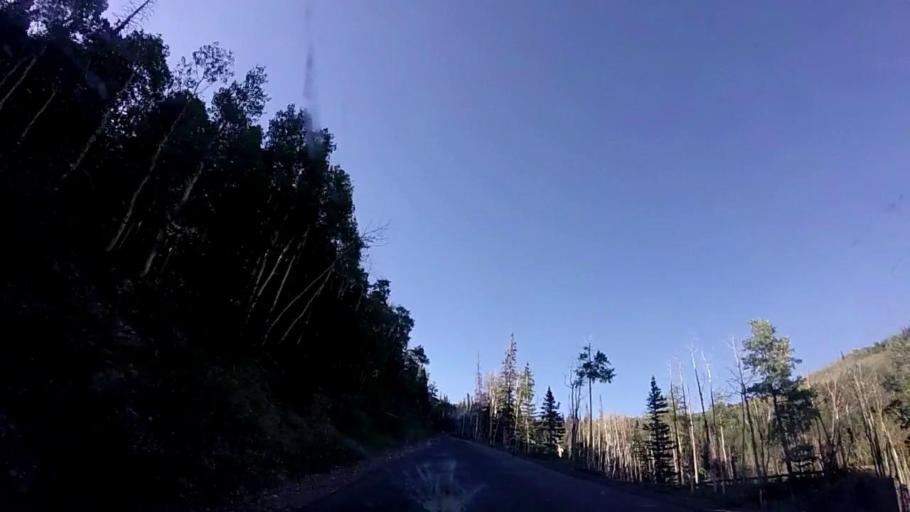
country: US
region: Utah
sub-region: Summit County
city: Park City
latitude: 40.6121
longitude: -111.5068
